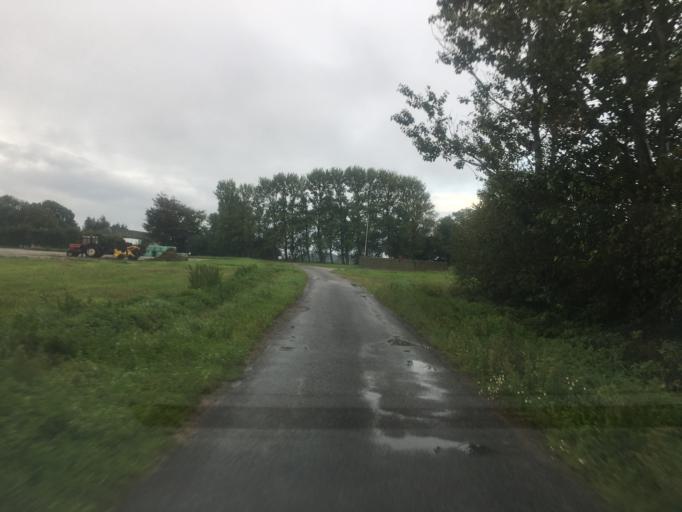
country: DK
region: South Denmark
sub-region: Tonder Kommune
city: Logumkloster
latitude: 54.9806
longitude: 8.9605
